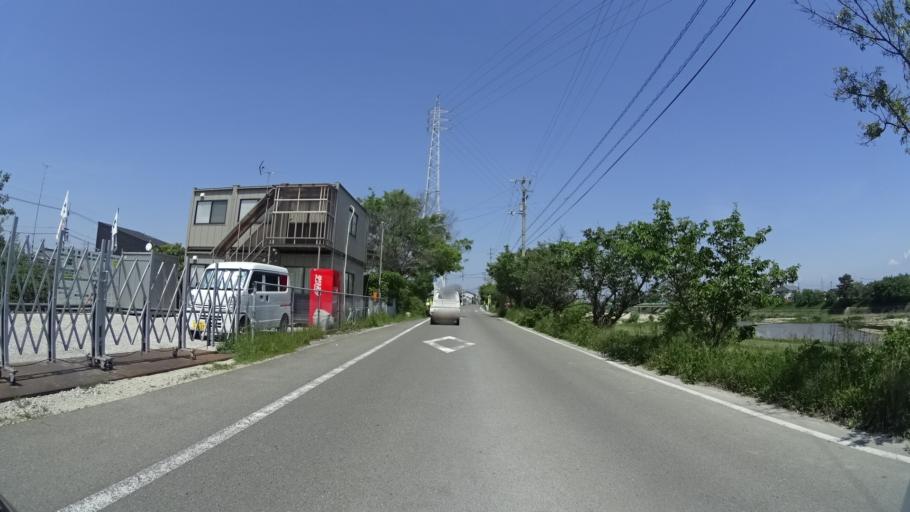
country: JP
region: Ehime
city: Hojo
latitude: 34.0536
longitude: 132.9942
